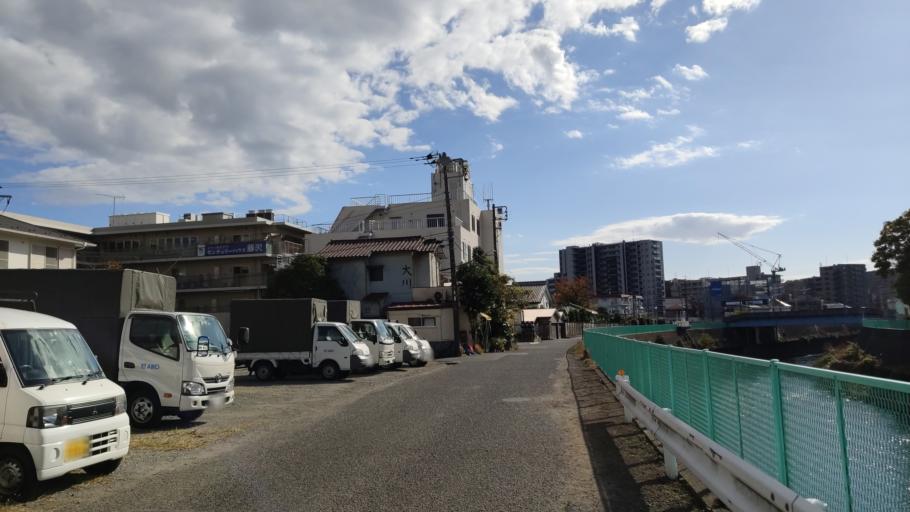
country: JP
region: Kanagawa
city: Fujisawa
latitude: 35.3392
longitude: 139.4943
